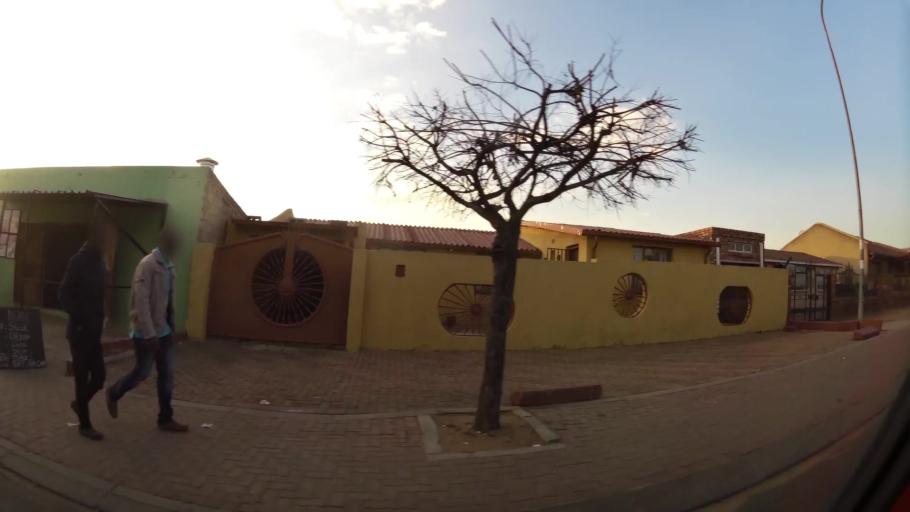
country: ZA
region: Gauteng
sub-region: City of Johannesburg Metropolitan Municipality
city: Soweto
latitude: -26.2222
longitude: 27.8949
